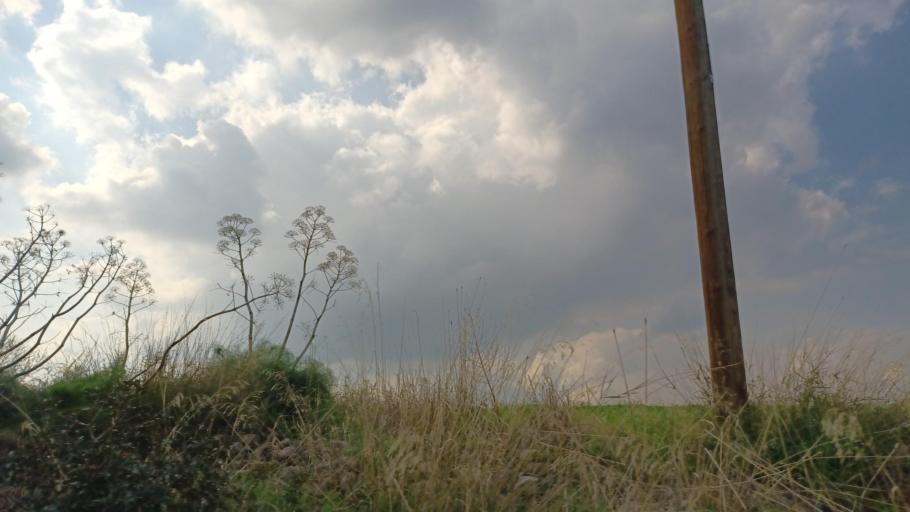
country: CY
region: Pafos
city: Polis
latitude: 35.0400
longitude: 32.4628
